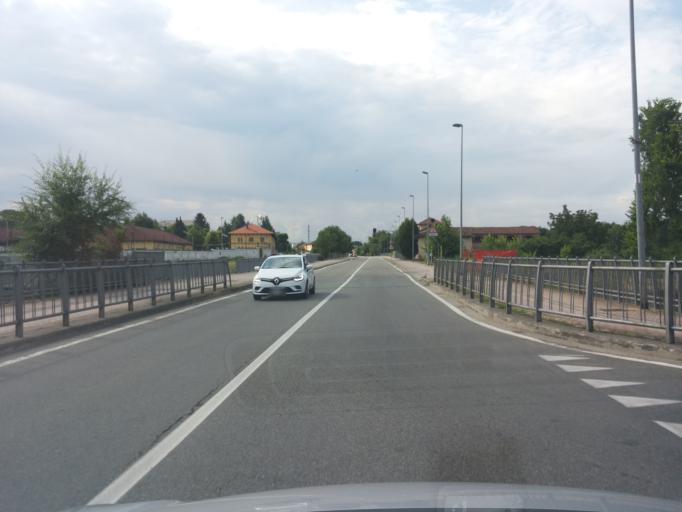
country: IT
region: Piedmont
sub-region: Provincia di Vercelli
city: Vercelli
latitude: 45.3086
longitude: 8.4420
